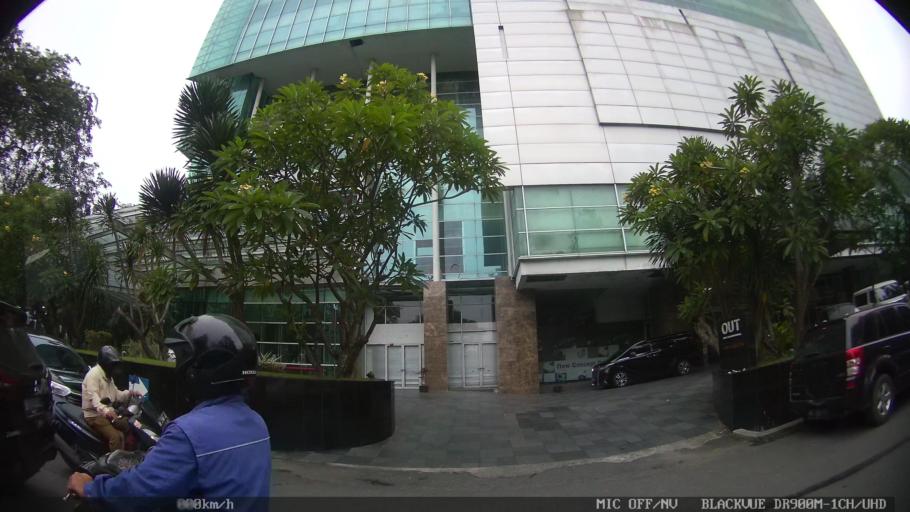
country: ID
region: North Sumatra
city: Medan
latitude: 3.5900
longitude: 98.6743
